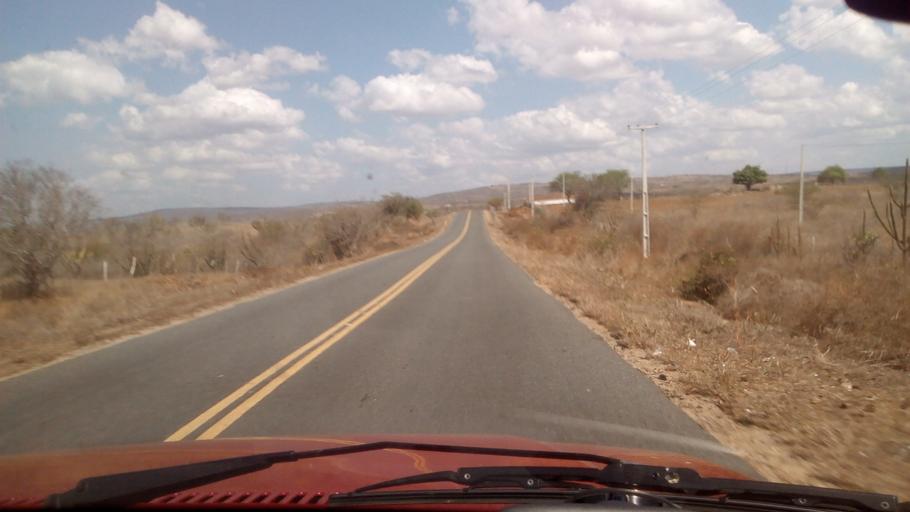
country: BR
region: Paraiba
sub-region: Cacimba De Dentro
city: Cacimba de Dentro
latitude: -6.6739
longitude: -35.7504
